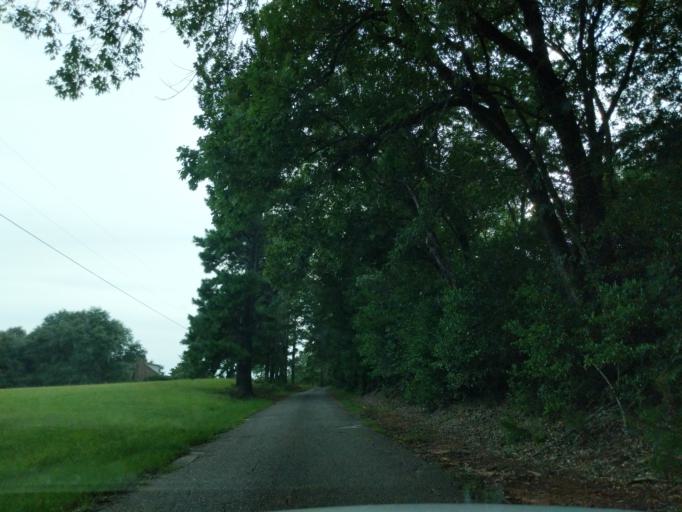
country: US
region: South Carolina
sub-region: Aiken County
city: North Augusta
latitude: 33.5327
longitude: -81.9901
